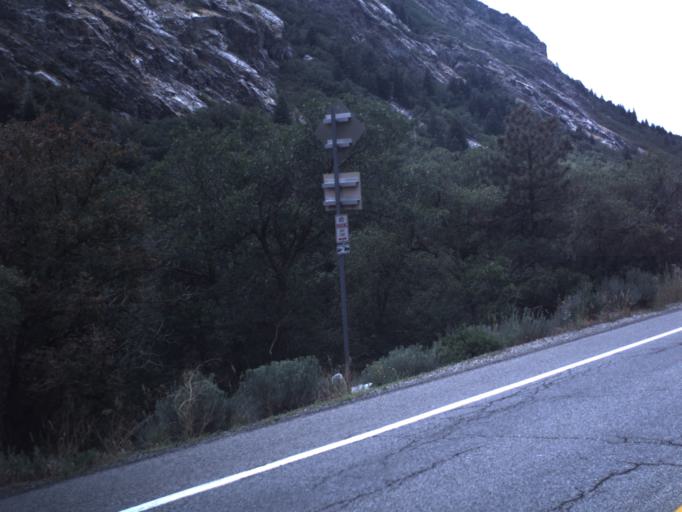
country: US
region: Utah
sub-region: Salt Lake County
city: Granite
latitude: 40.5720
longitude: -111.7731
